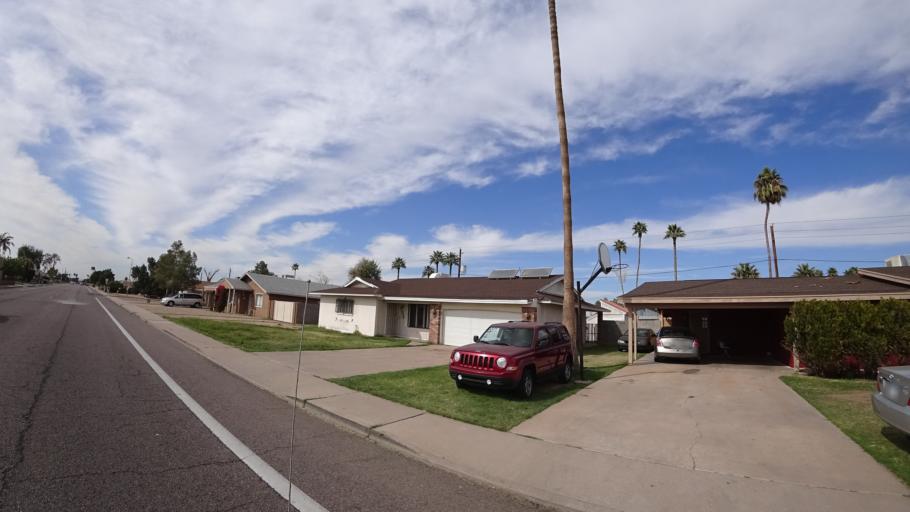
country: US
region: Arizona
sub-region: Maricopa County
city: Glendale
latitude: 33.4732
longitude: -112.1734
